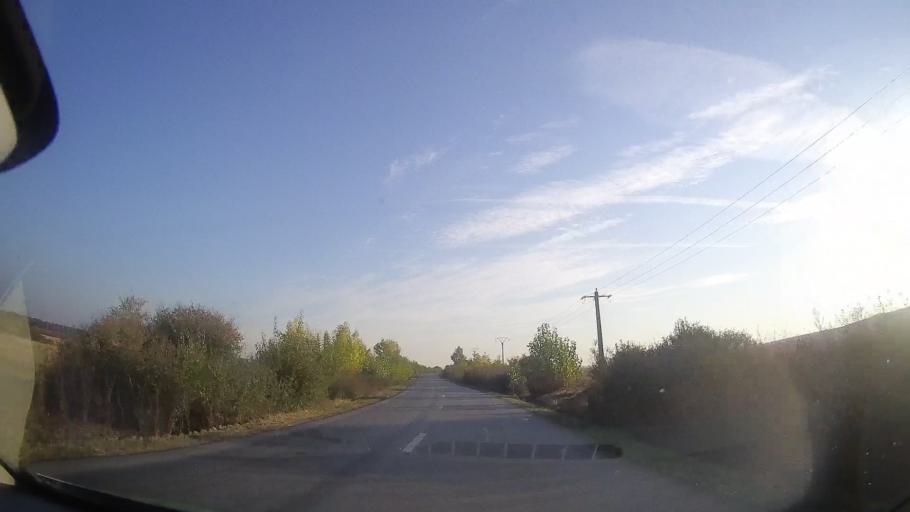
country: RO
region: Timis
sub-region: Comuna Pischia
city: Pischia
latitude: 45.8780
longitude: 21.3337
